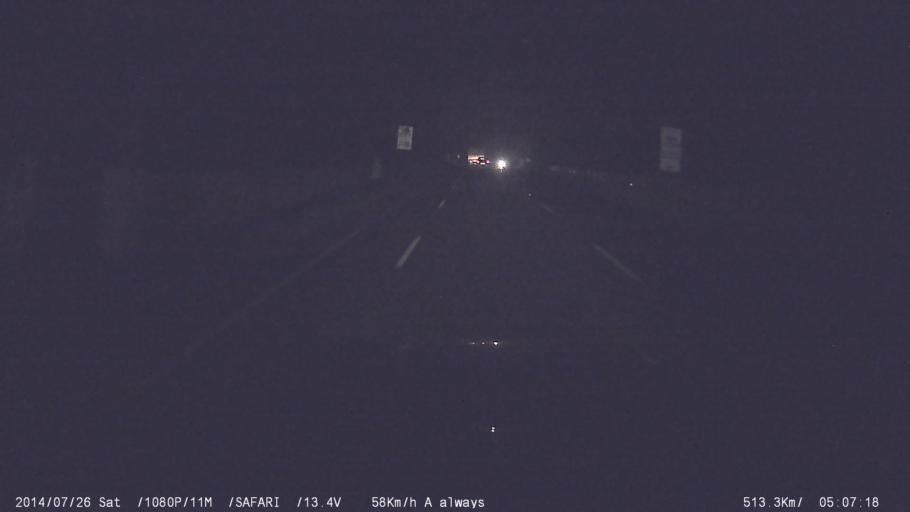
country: IN
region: Kerala
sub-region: Ernakulam
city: Perumbavoor
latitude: 10.0730
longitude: 76.5086
